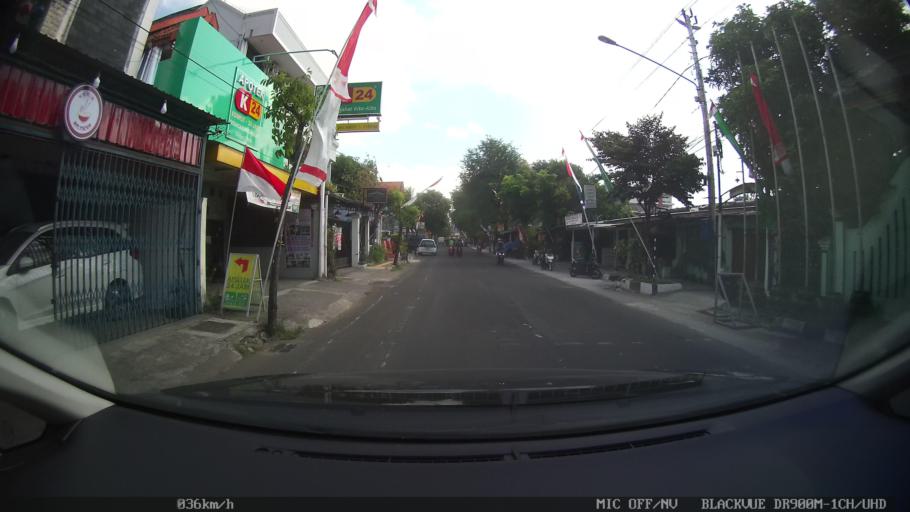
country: ID
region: Daerah Istimewa Yogyakarta
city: Yogyakarta
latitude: -7.8176
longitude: 110.3732
